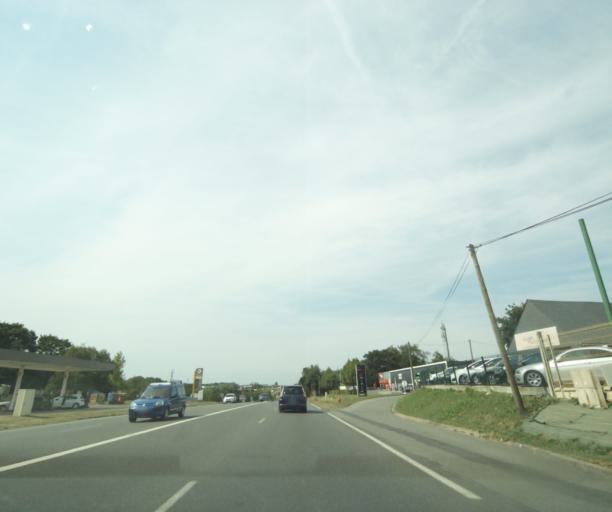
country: FR
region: Centre
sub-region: Departement d'Indre-et-Loire
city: Chambray-les-Tours
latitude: 47.3160
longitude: 0.7113
